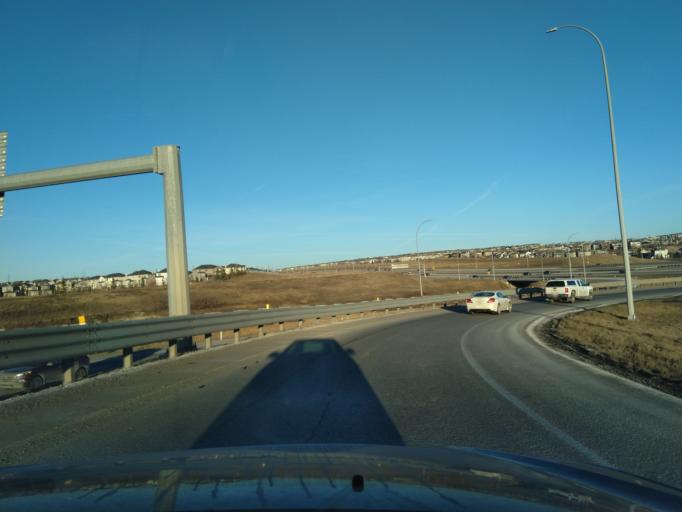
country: CA
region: Alberta
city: Calgary
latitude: 51.1583
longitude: -114.1171
